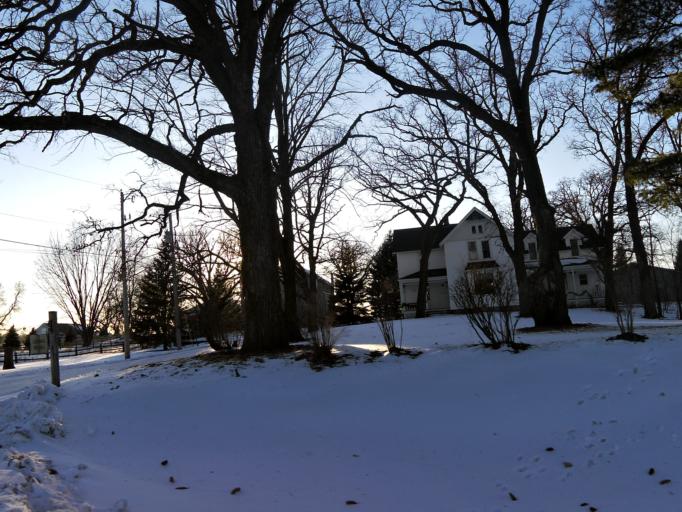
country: US
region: Minnesota
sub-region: Washington County
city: Lake Elmo
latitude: 44.9820
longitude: -92.8430
